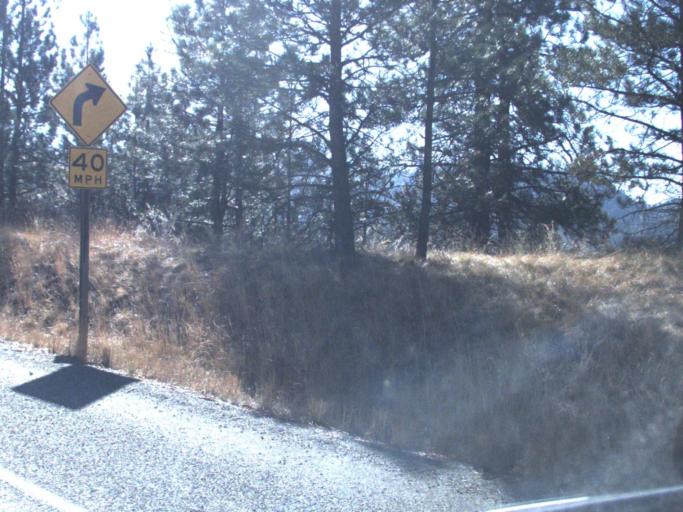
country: US
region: Washington
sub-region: Ferry County
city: Republic
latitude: 48.6675
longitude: -118.6671
